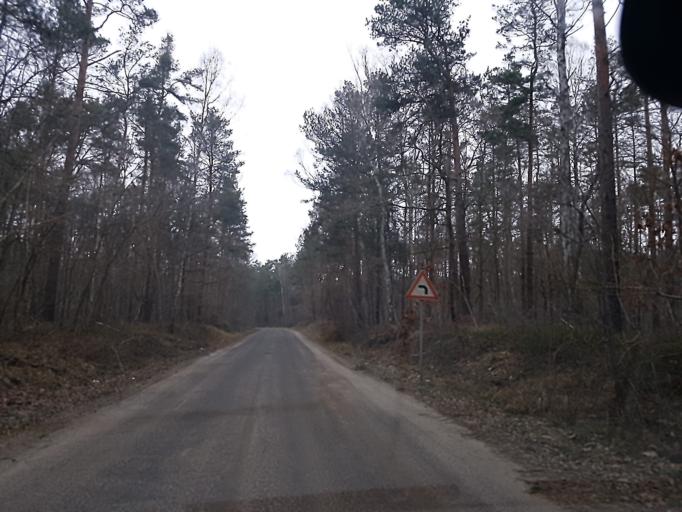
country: DE
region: Brandenburg
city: Ruckersdorf
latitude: 51.5954
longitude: 13.5657
